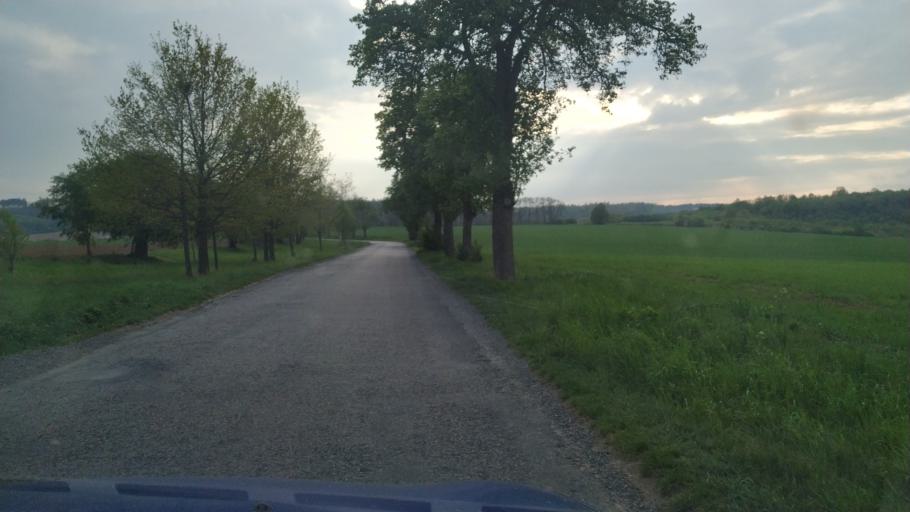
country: CZ
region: Olomoucky
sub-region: Okres Olomouc
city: Slatinice
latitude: 49.5522
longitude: 17.1000
